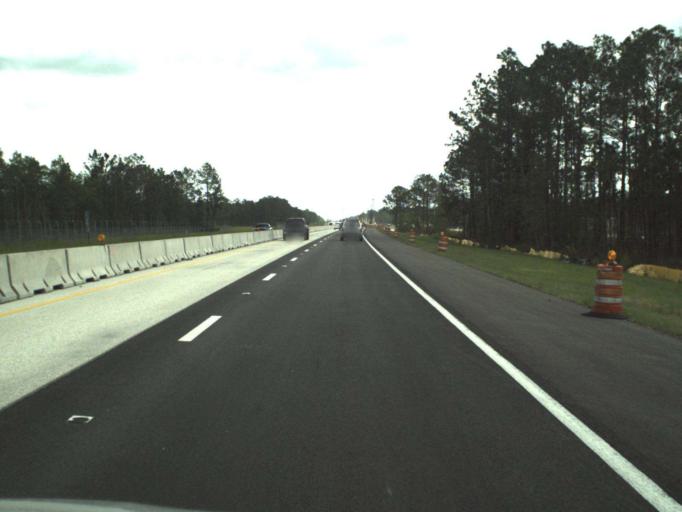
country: US
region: Florida
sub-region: Volusia County
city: Samsula-Spruce Creek
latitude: 29.0932
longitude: -81.1605
